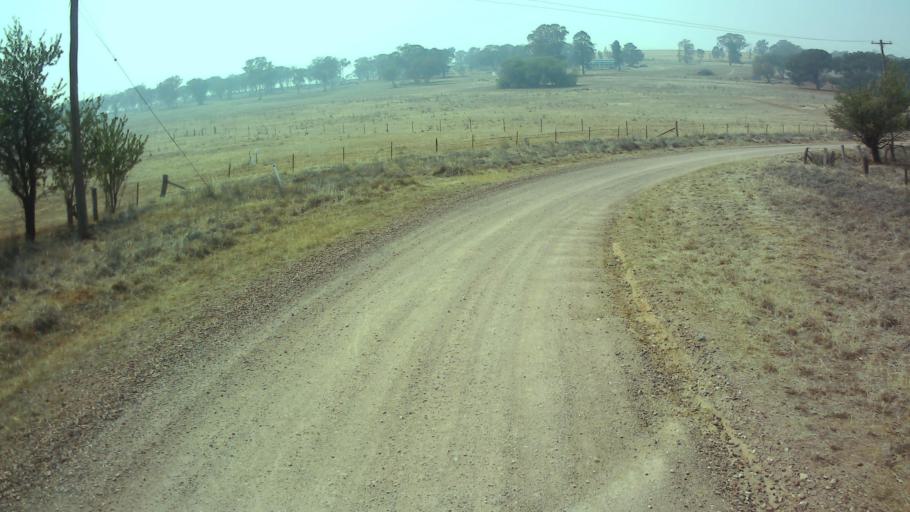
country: AU
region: New South Wales
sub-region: Weddin
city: Grenfell
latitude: -33.9058
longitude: 148.1731
